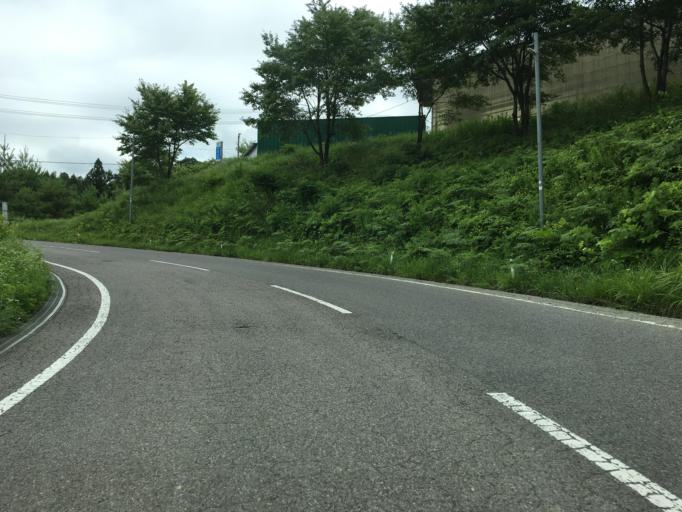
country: JP
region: Fukushima
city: Nihommatsu
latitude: 37.5754
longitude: 140.4283
